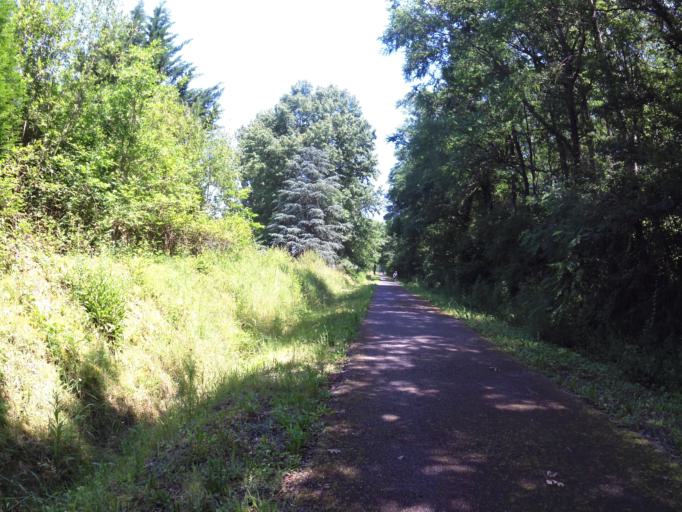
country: FR
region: Aquitaine
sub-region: Departement des Pyrenees-Atlantiques
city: Salies-de-Bearn
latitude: 43.4656
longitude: -0.9520
